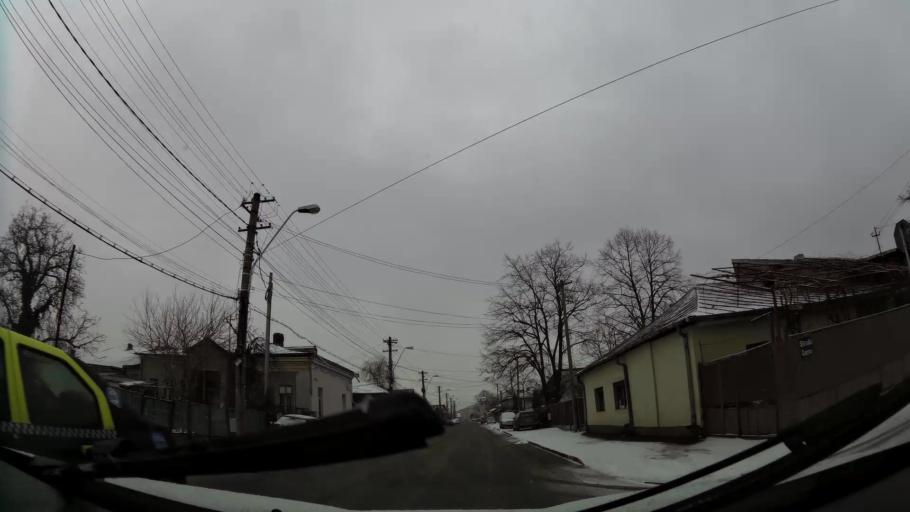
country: RO
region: Prahova
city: Ploiesti
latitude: 44.9289
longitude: 26.0177
